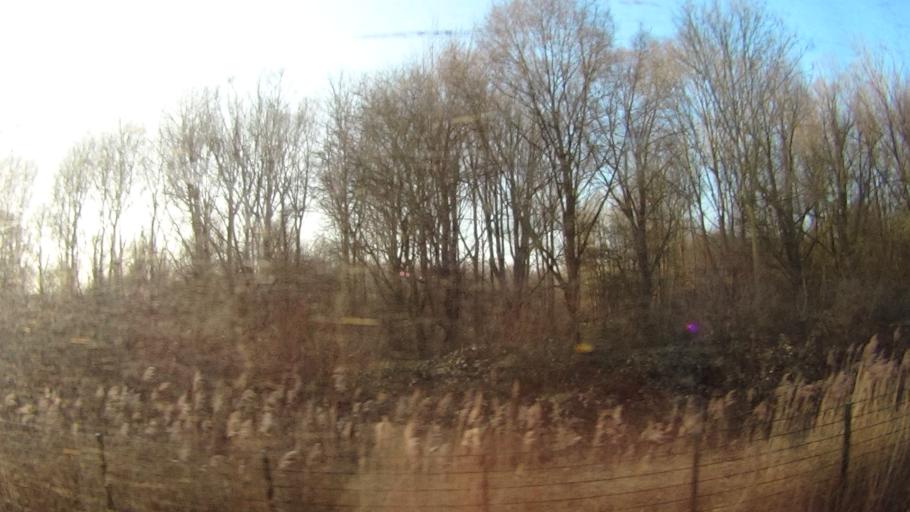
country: NL
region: Overijssel
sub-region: Gemeente Zwolle
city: Zwolle
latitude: 52.5009
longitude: 6.0767
